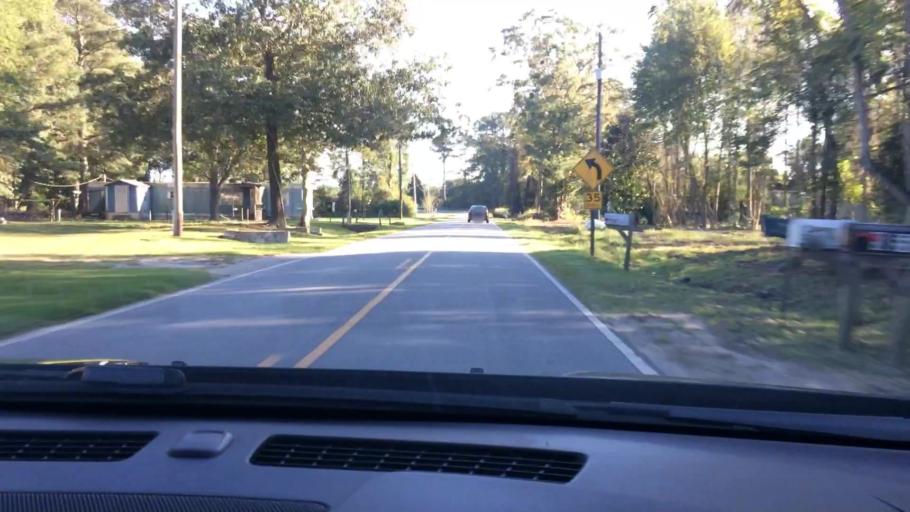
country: US
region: North Carolina
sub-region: Pitt County
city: Ayden
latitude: 35.4987
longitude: -77.4337
